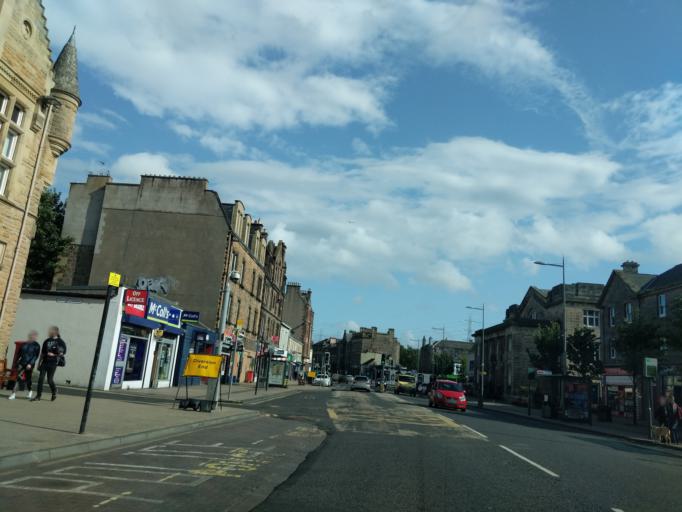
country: GB
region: Scotland
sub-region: West Lothian
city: Seafield
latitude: 55.9537
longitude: -3.1157
